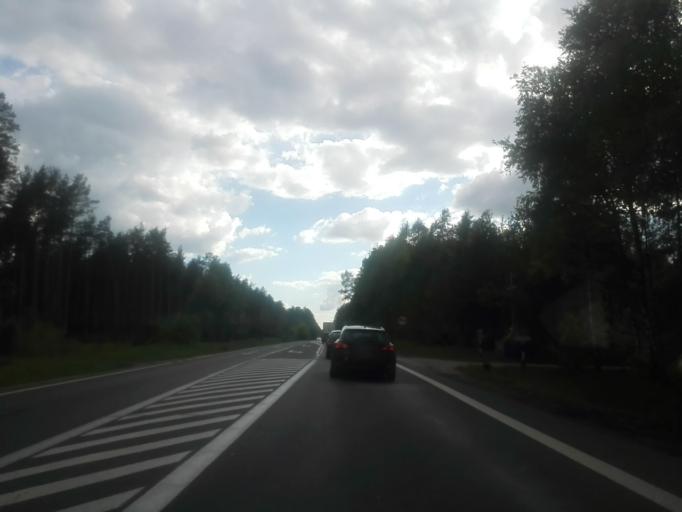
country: PL
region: Masovian Voivodeship
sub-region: Powiat ostrowski
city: Brok
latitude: 52.7366
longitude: 21.7480
